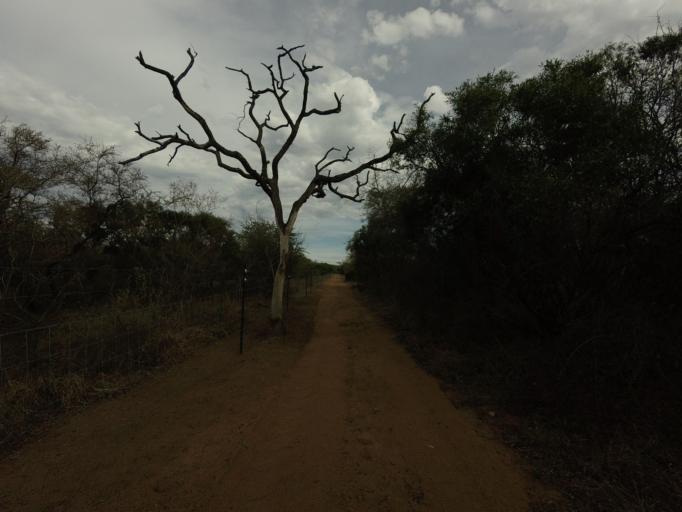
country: ZA
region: Limpopo
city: Thulamahashi
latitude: -24.5217
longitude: 31.1186
